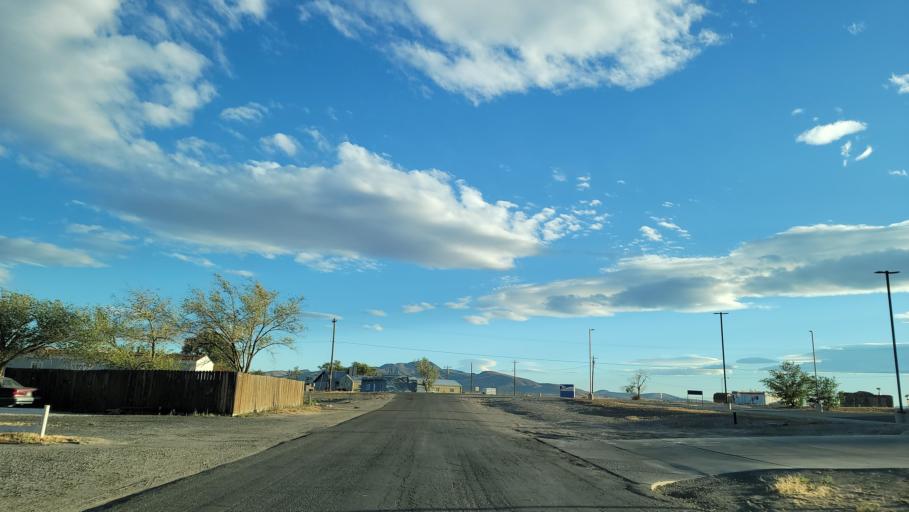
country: US
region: Nevada
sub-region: Lyon County
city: Silver Springs
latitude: 39.4150
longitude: -119.2230
